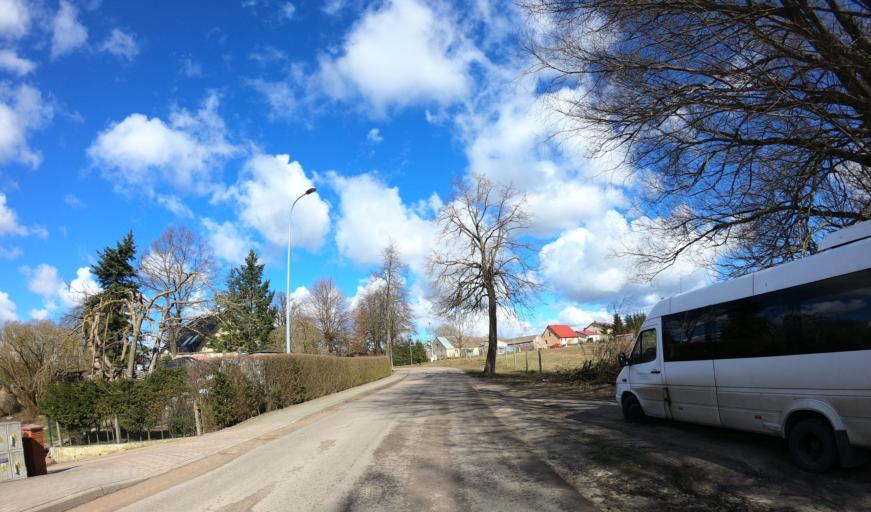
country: PL
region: West Pomeranian Voivodeship
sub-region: Powiat drawski
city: Drawsko Pomorskie
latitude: 53.4888
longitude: 15.8649
